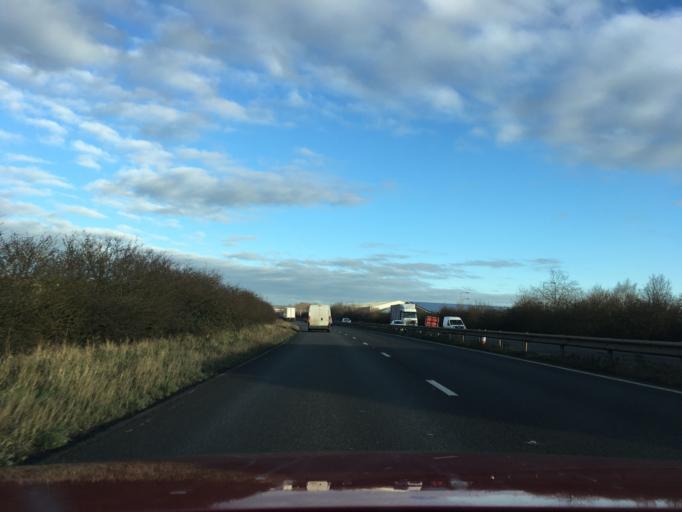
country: GB
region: England
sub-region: Staffordshire
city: Burton upon Trent
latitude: 52.7949
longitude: -1.6707
